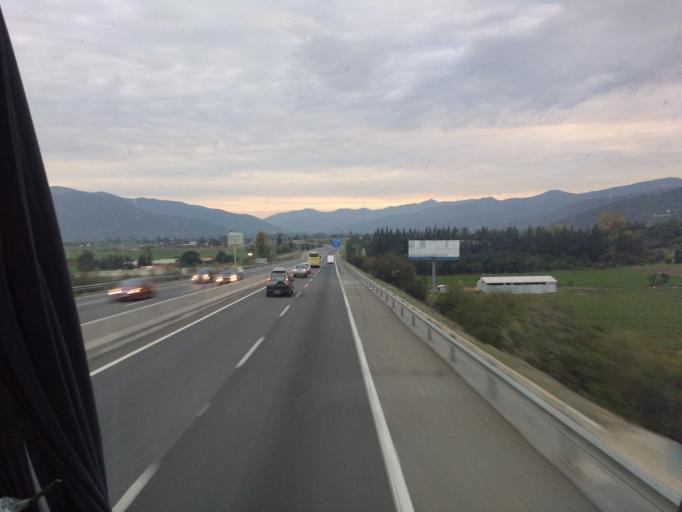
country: CL
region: Santiago Metropolitan
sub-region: Provincia de Chacabuco
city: Lampa
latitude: -33.4401
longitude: -71.0194
